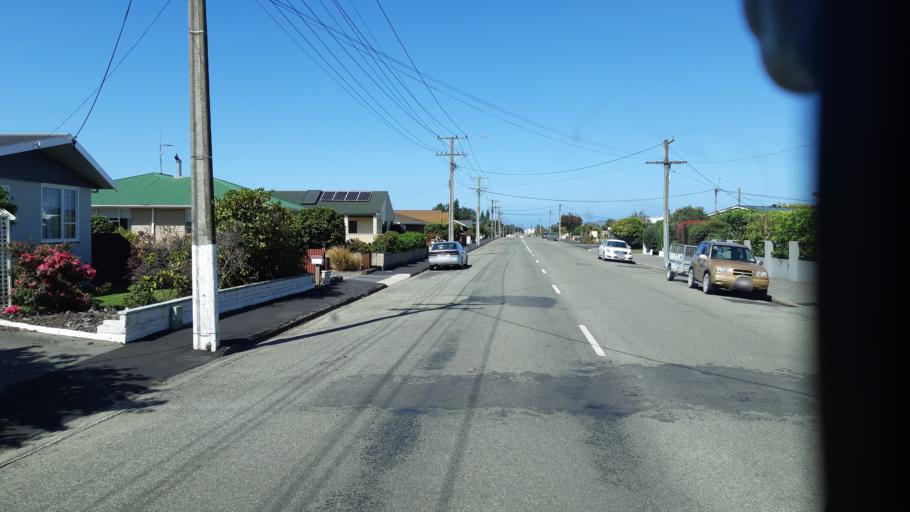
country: NZ
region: Otago
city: Oamaru
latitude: -45.0672
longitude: 170.9897
